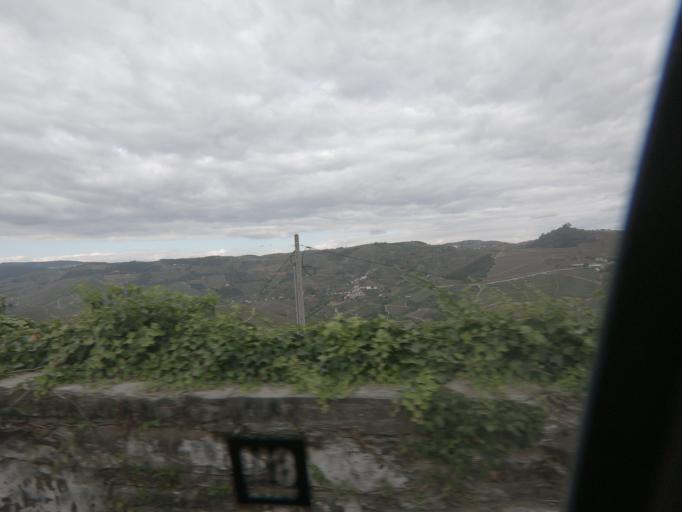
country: PT
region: Vila Real
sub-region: Sabrosa
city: Vilela
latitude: 41.2184
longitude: -7.5538
